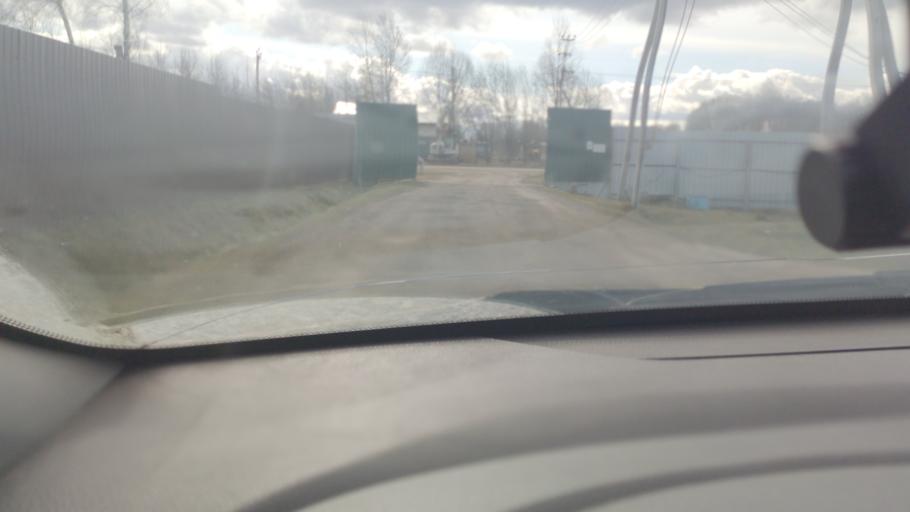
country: RU
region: Moskovskaya
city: Ruza
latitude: 55.7628
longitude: 36.1378
